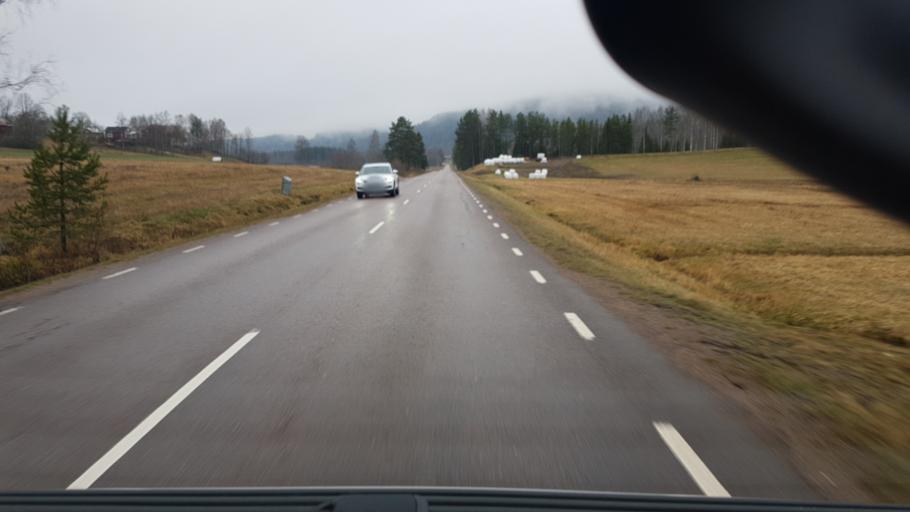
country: SE
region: Vaermland
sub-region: Arvika Kommun
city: Arvika
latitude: 59.7380
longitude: 12.6412
